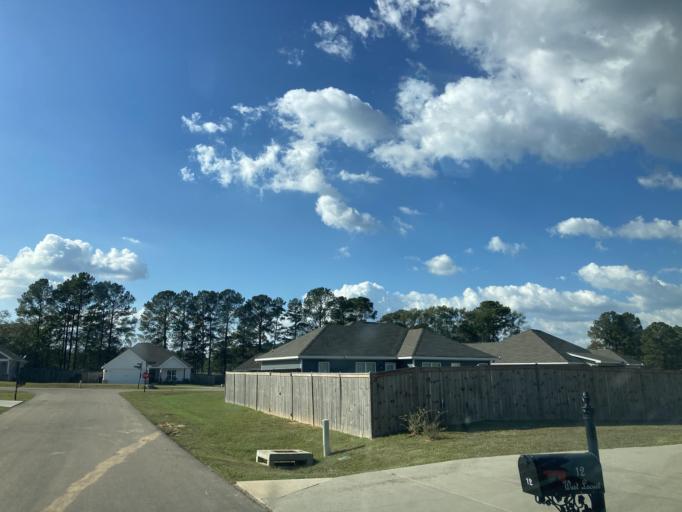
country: US
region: Mississippi
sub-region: Lamar County
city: Sumrall
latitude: 31.4289
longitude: -89.5344
